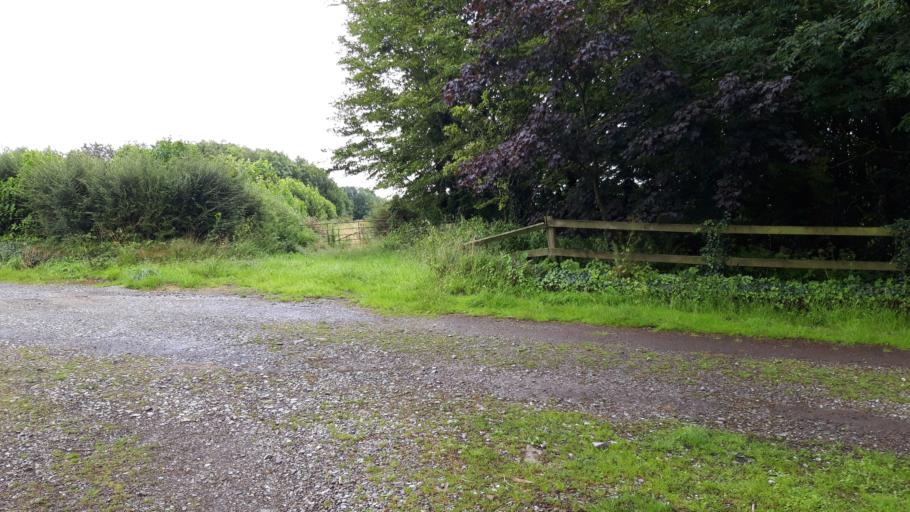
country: IE
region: Munster
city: Cahir
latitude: 52.1865
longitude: -7.8581
